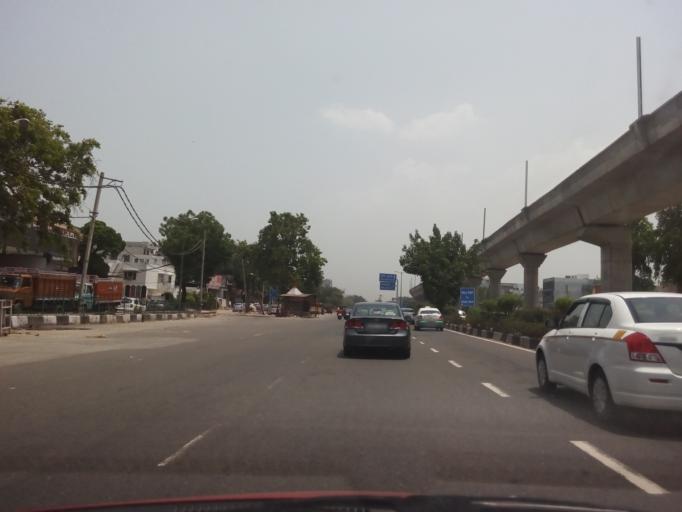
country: IN
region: NCT
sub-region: North West Delhi
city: Pitampura
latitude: 28.6423
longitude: 77.1282
